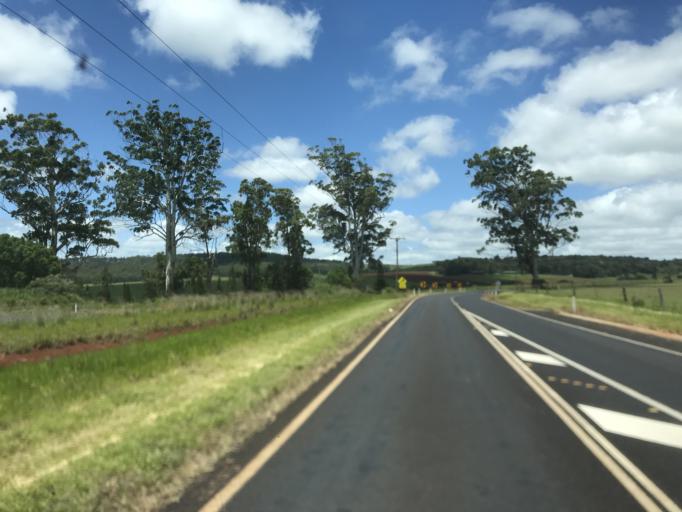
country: AU
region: Queensland
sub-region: Tablelands
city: Ravenshoe
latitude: -17.5087
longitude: 145.4559
